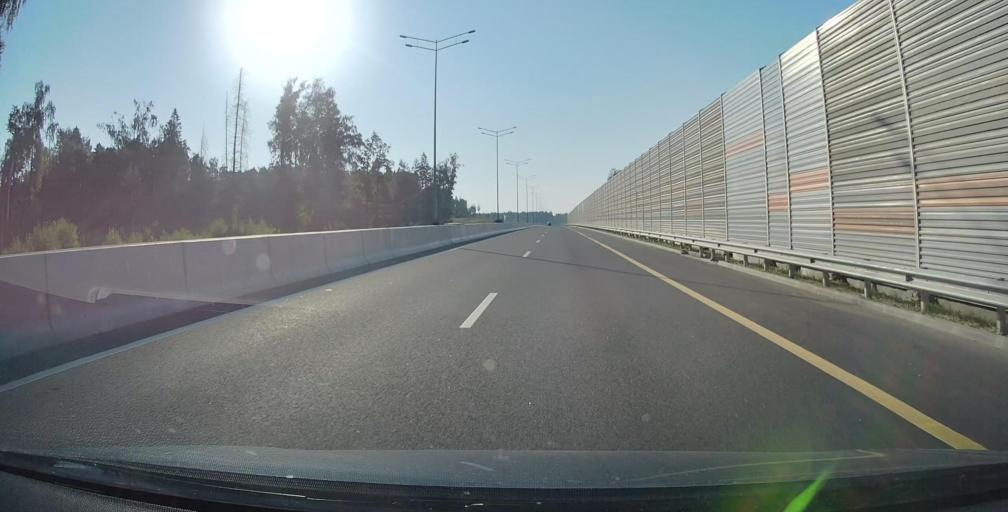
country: RU
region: Moskovskaya
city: Yel'digino
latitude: 56.1489
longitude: 37.7931
